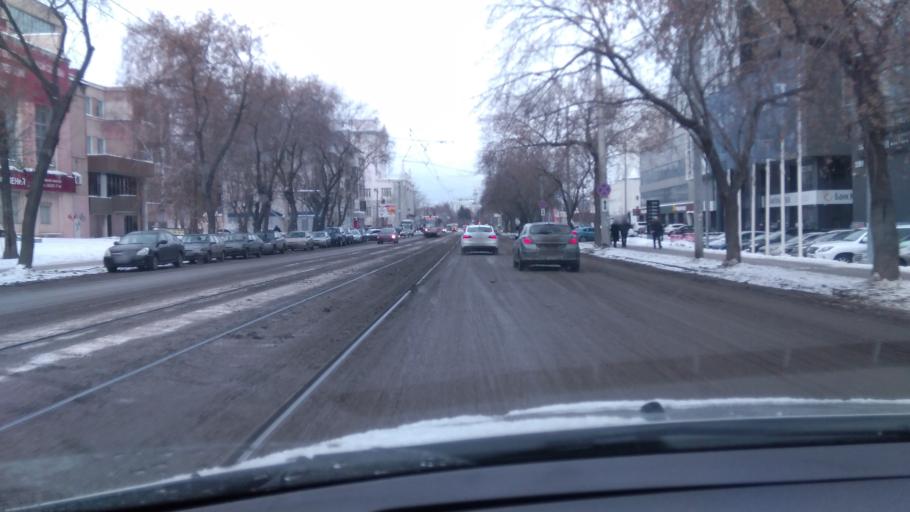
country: RU
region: Sverdlovsk
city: Yekaterinburg
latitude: 56.8232
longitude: 60.6046
